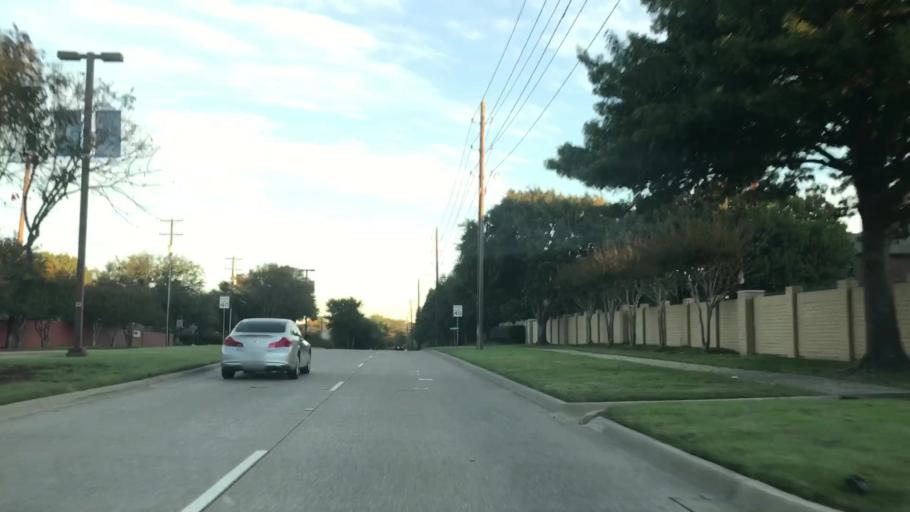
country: US
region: Texas
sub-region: Dallas County
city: Addison
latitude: 33.0137
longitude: -96.8572
